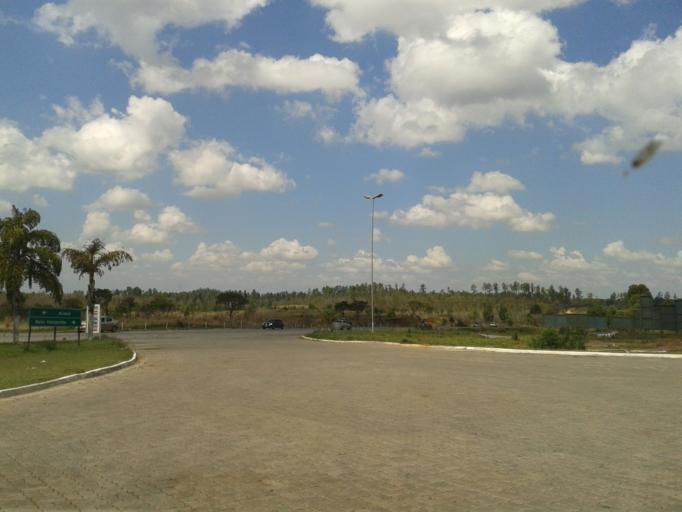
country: BR
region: Minas Gerais
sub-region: Campos Altos
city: Campos Altos
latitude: -19.6689
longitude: -46.0521
